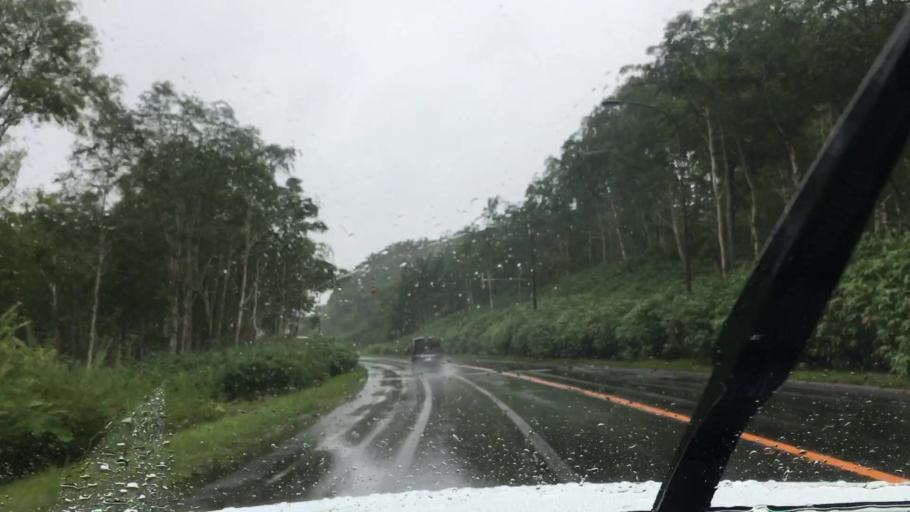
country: JP
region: Hokkaido
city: Sapporo
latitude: 42.8625
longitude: 141.1043
